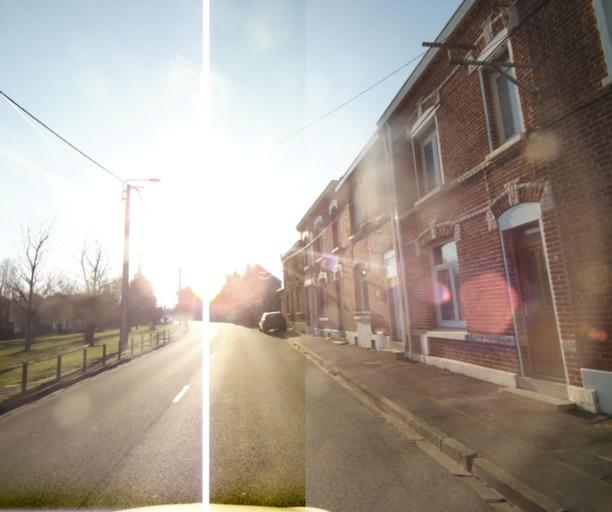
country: FR
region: Nord-Pas-de-Calais
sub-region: Departement du Nord
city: Valenciennes
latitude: 50.3451
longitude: 3.5320
